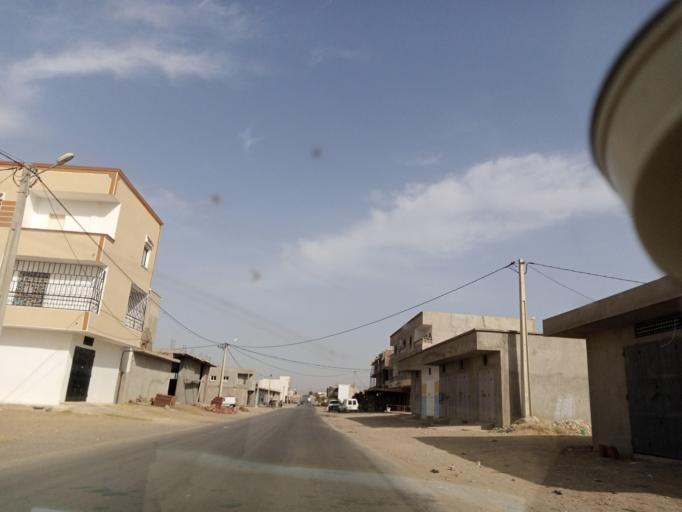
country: TN
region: Al Qasrayn
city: Kasserine
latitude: 35.2143
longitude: 8.9020
